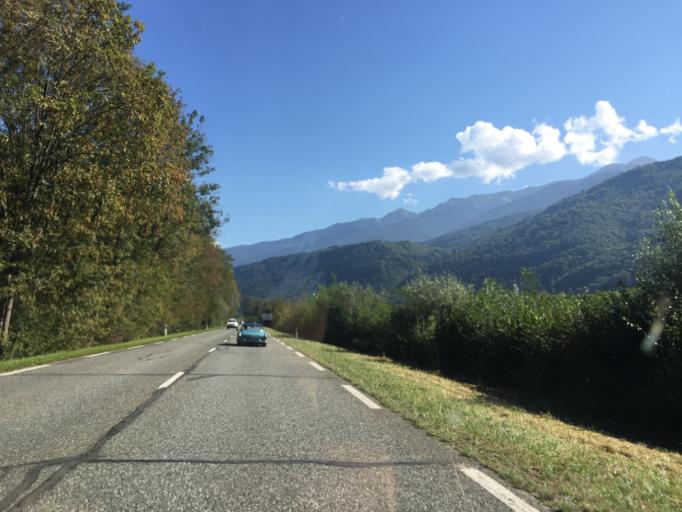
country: FR
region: Rhone-Alpes
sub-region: Departement de la Savoie
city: Aiton
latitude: 45.5806
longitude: 6.2613
